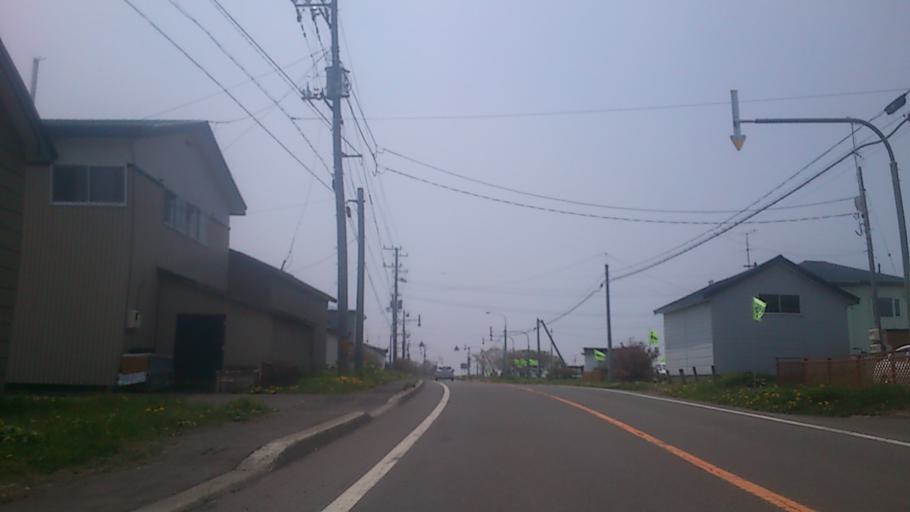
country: JP
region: Hokkaido
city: Nemuro
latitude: 43.3409
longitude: 145.7385
